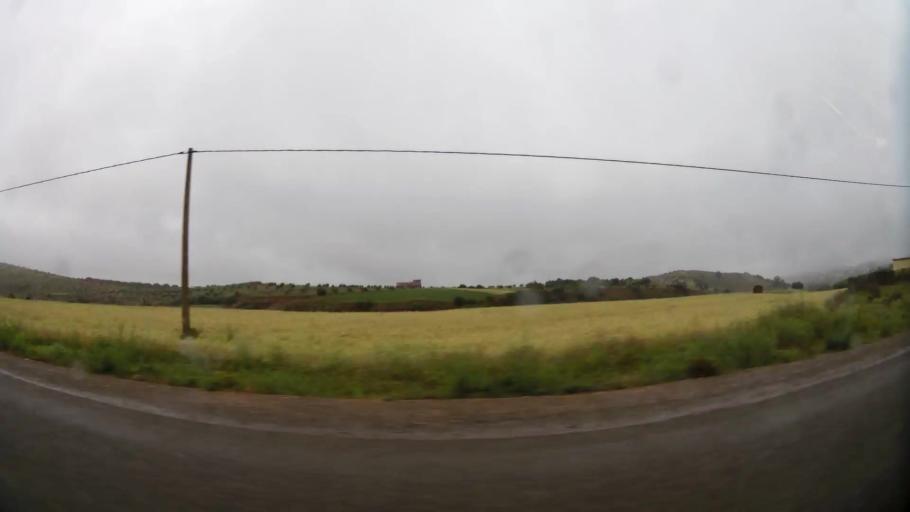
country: MA
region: Oriental
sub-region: Nador
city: Boudinar
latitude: 35.1161
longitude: -3.5767
